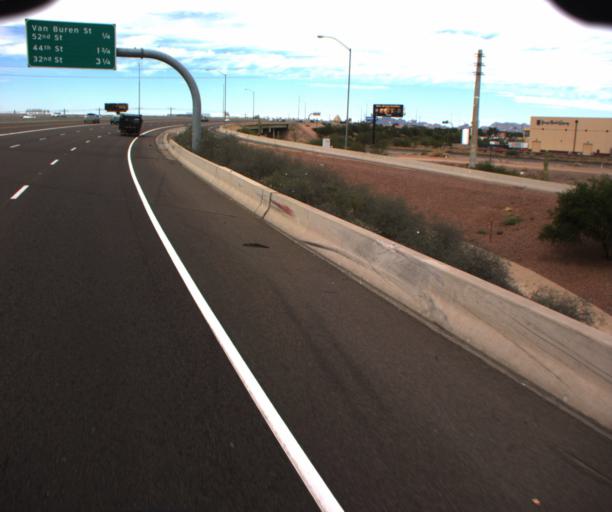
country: US
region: Arizona
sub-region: Maricopa County
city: Tempe Junction
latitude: 33.4397
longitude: -111.9665
